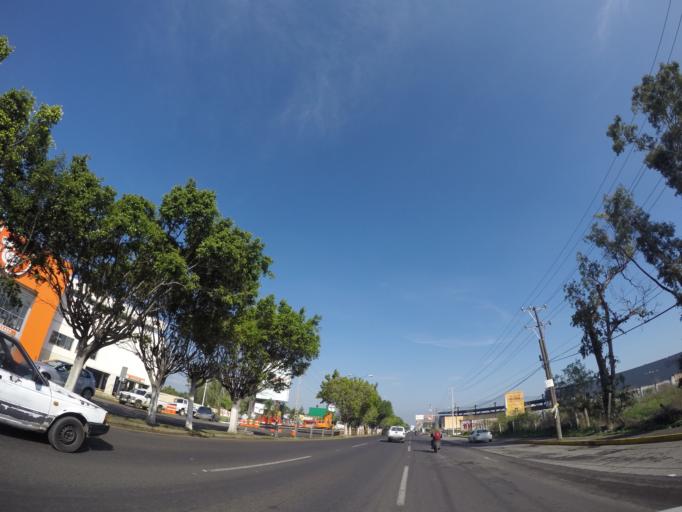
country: MX
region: Michoacan
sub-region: Morelia
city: Morelos
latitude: 19.6730
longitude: -101.2114
